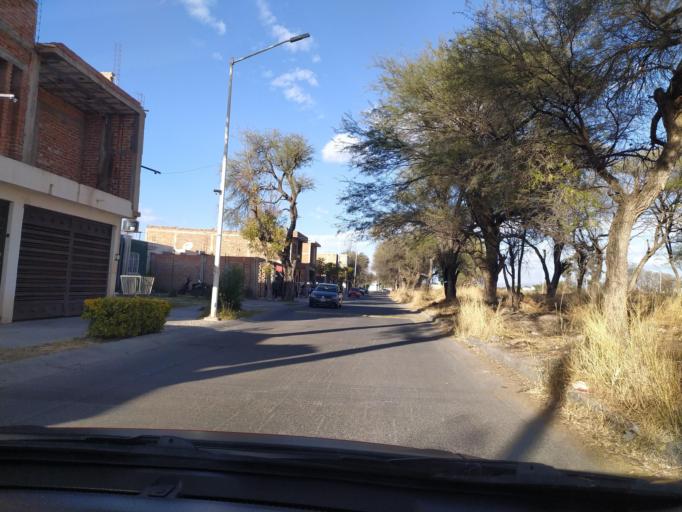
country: MX
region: Guanajuato
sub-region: Purisima del Rincon
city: Monte Grande
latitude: 21.0061
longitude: -101.8718
